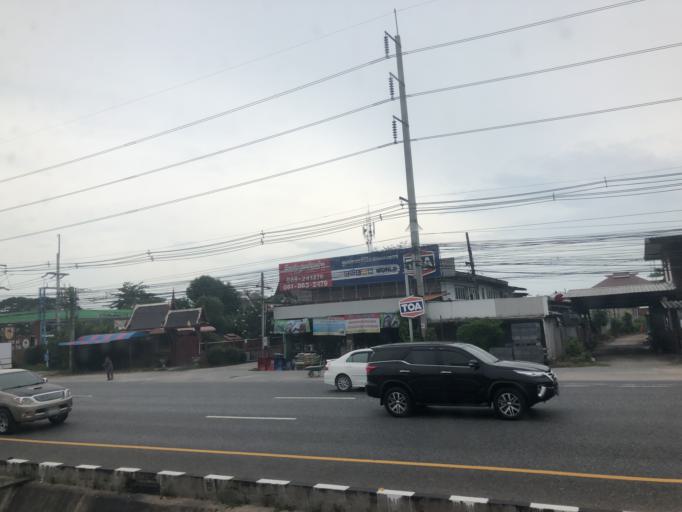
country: TH
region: Chon Buri
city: Bang Lamung
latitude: 13.0420
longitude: 100.9271
